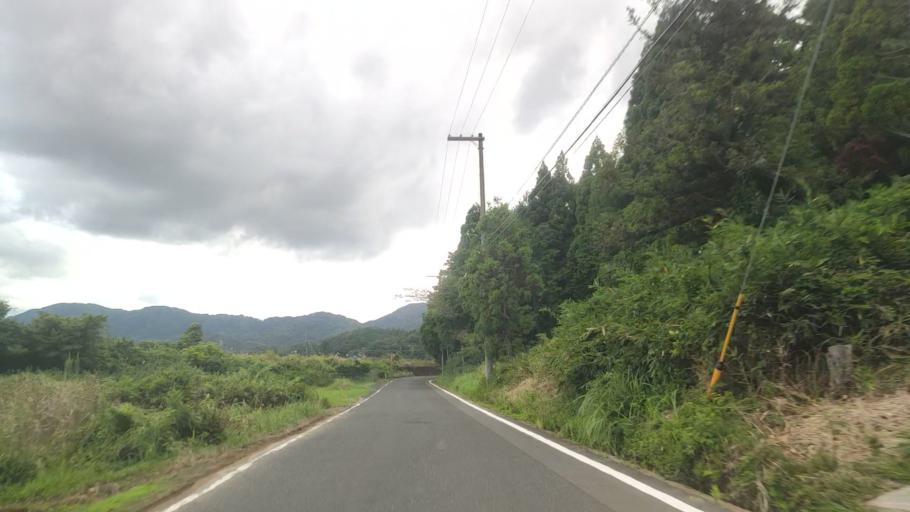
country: JP
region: Hyogo
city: Toyooka
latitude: 35.6006
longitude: 134.8880
